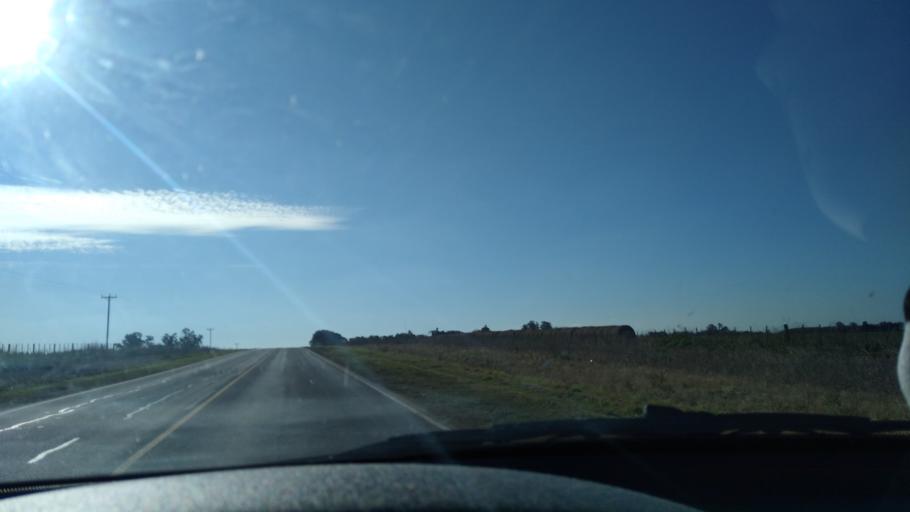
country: AR
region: Entre Rios
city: Aranguren
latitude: -32.3949
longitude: -60.3293
